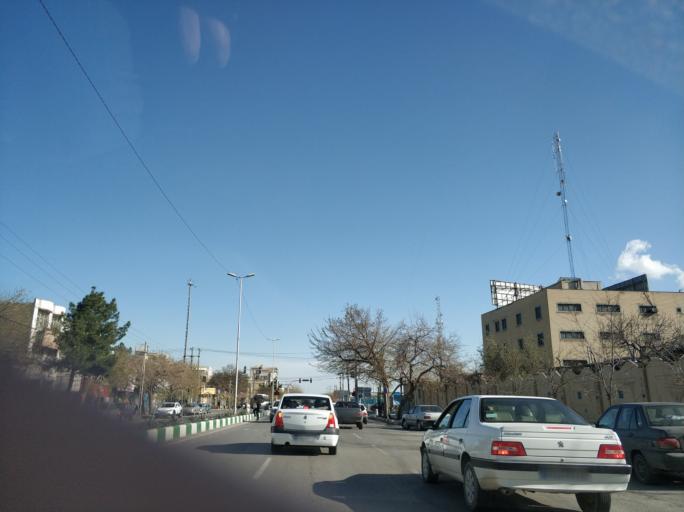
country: IR
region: Razavi Khorasan
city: Mashhad
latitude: 36.2999
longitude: 59.6329
